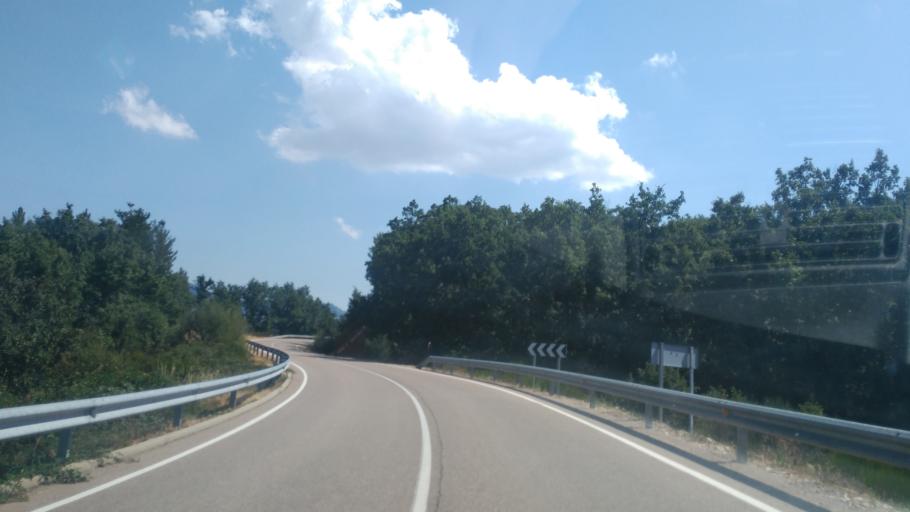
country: ES
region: Castille and Leon
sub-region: Provincia de Salamanca
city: Cereceda de la Sierra
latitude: 40.5666
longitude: -6.1118
